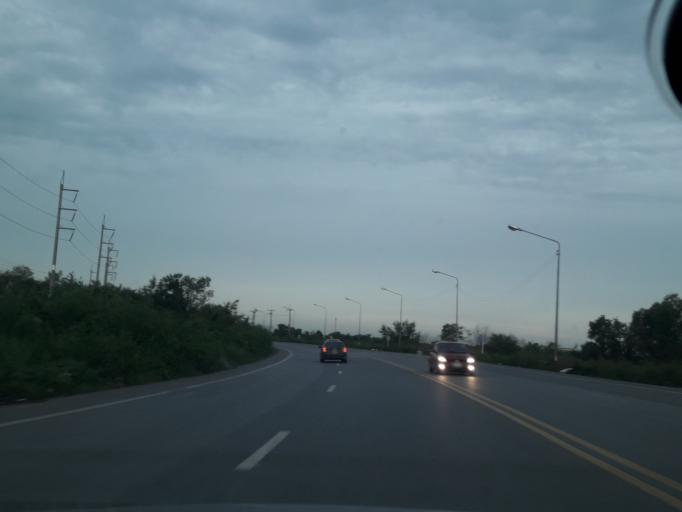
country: TH
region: Pathum Thani
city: Ban Rangsit
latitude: 14.0191
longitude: 100.7488
